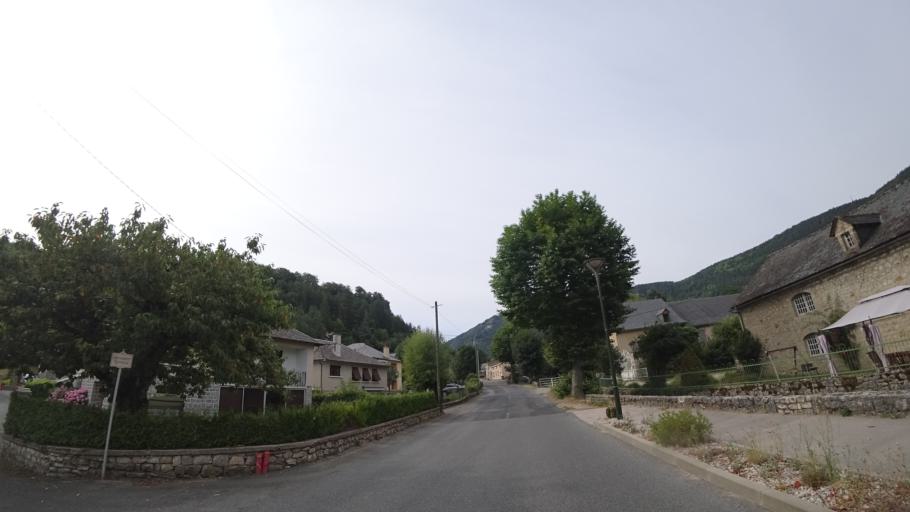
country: FR
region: Languedoc-Roussillon
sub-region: Departement de la Lozere
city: La Canourgue
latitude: 44.4279
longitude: 3.2223
